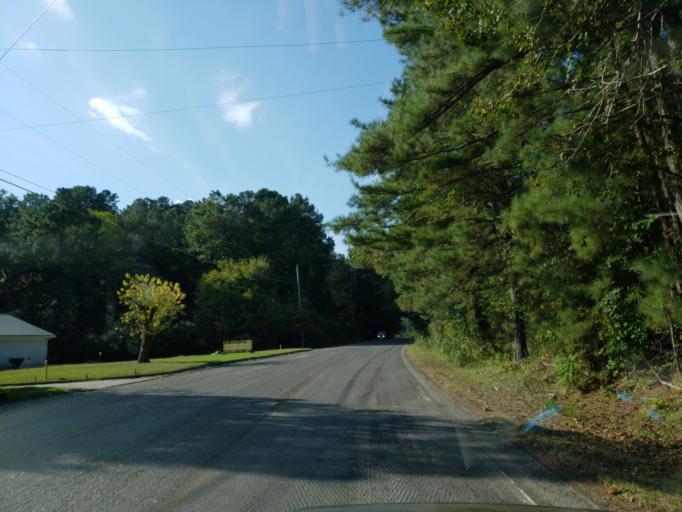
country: US
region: Georgia
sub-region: Cobb County
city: Powder Springs
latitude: 33.8710
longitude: -84.7126
